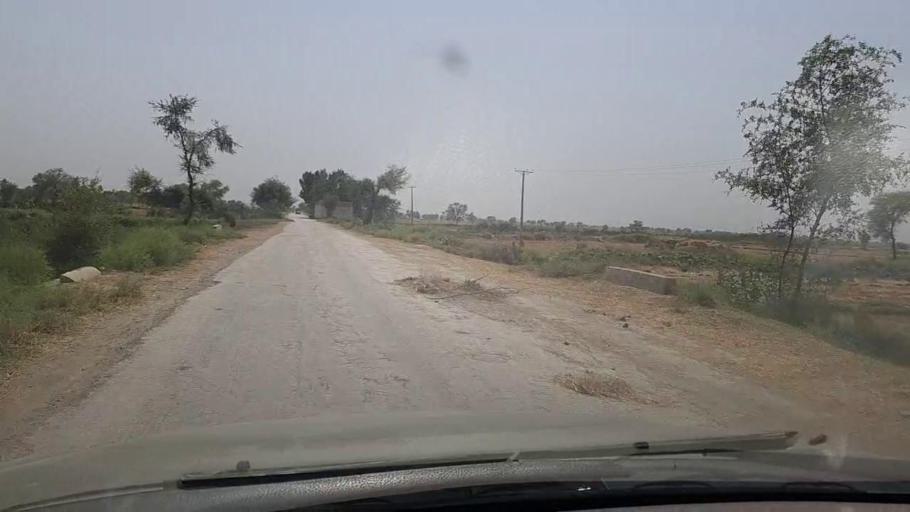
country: PK
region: Sindh
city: Miro Khan
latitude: 27.7179
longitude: 68.0677
